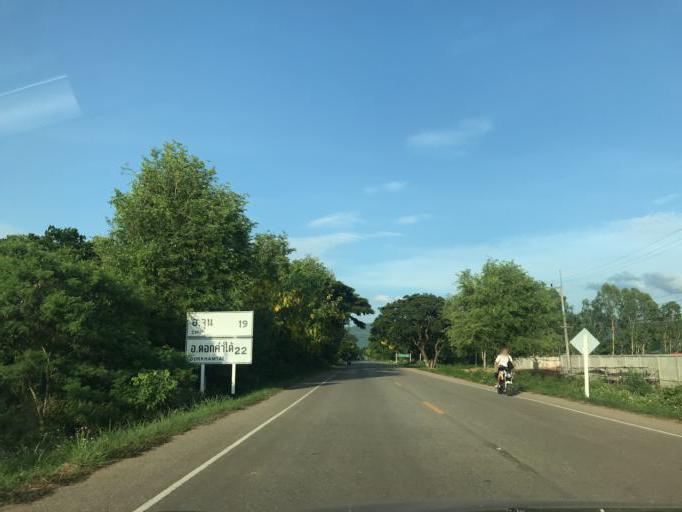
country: TH
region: Phayao
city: Phu Kam Yao
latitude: 19.3126
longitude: 100.0061
